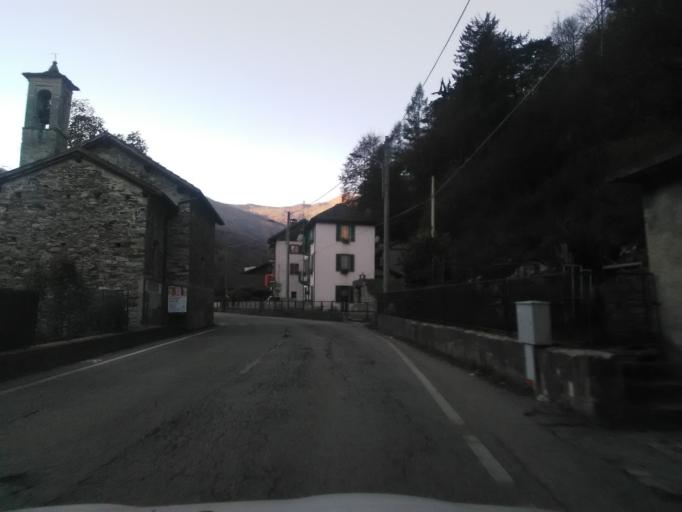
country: IT
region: Piedmont
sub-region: Provincia di Vercelli
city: Scopa
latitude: 45.7867
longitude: 8.1089
